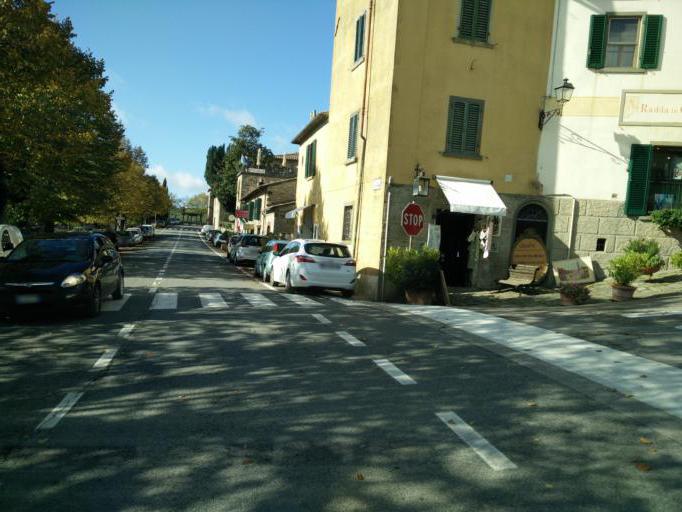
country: IT
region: Tuscany
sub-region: Provincia di Siena
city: Radda in Chianti
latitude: 43.4869
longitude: 11.3758
